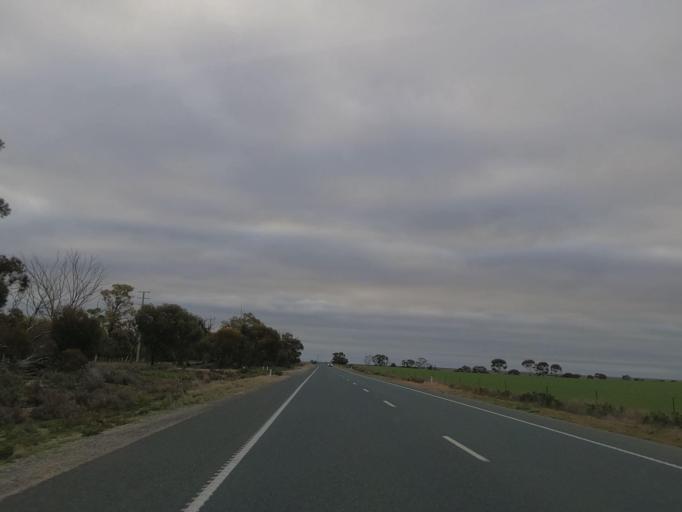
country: AU
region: Victoria
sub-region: Swan Hill
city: Swan Hill
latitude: -35.5587
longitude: 143.7796
